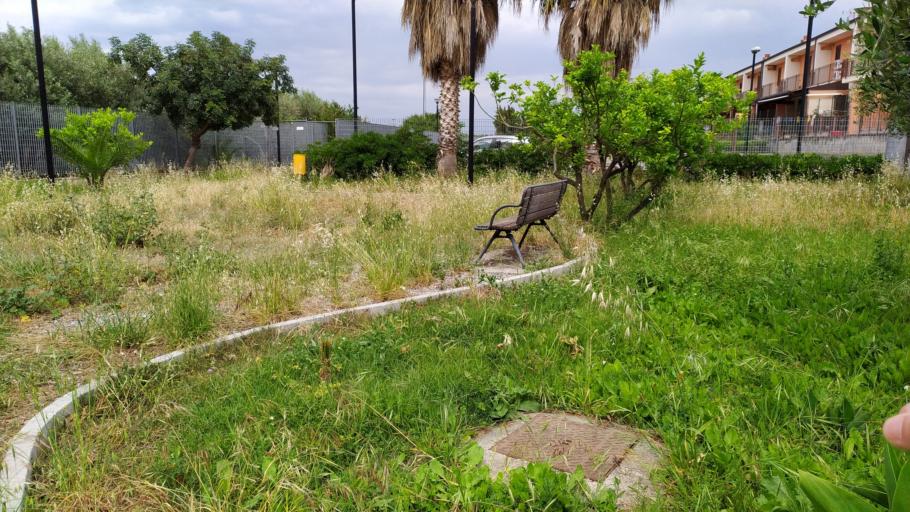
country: IT
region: Sicily
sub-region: Messina
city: Milazzo
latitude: 38.1943
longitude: 15.2520
